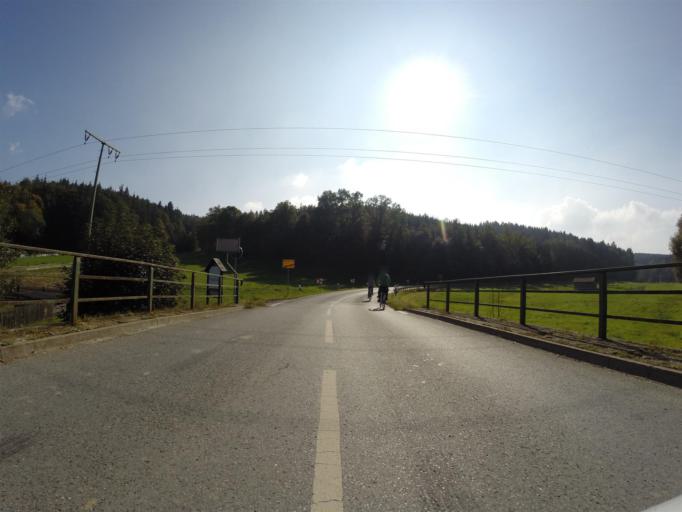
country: DE
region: Thuringia
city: Geisenhain
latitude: 50.8347
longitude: 11.7156
